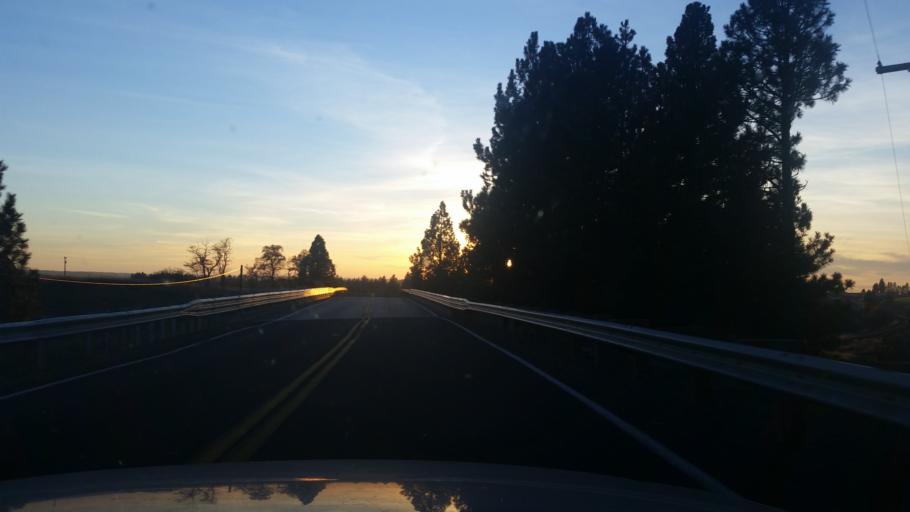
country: US
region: Washington
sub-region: Spokane County
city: Veradale
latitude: 47.5074
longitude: -117.1515
